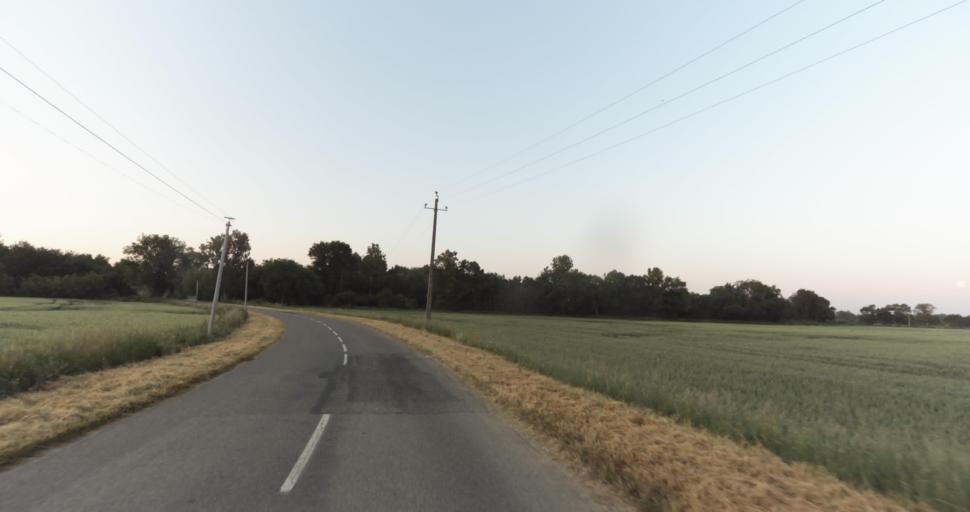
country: FR
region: Midi-Pyrenees
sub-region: Departement de la Haute-Garonne
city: Levignac
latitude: 43.6516
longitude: 1.1502
